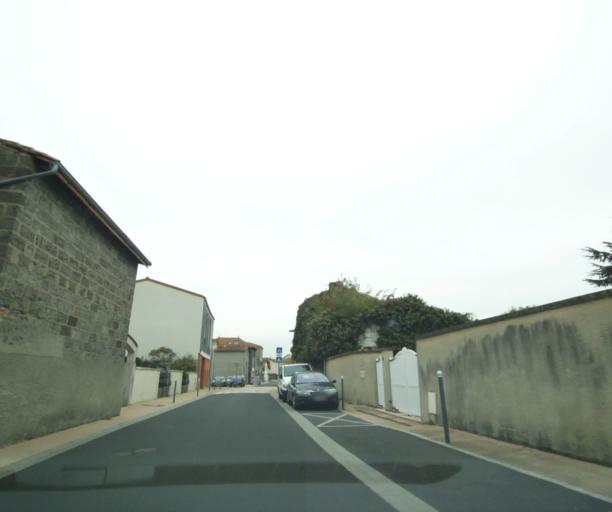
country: FR
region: Auvergne
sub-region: Departement du Puy-de-Dome
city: Gerzat
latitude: 45.8279
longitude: 3.1459
